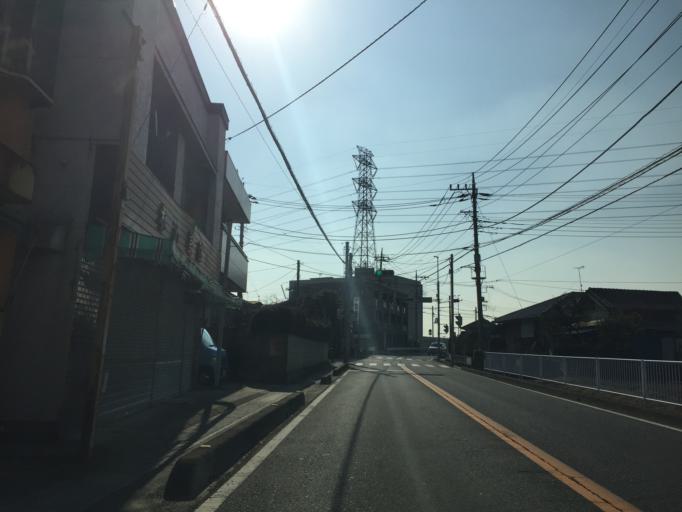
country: JP
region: Saitama
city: Shiki
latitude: 35.8431
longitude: 139.5831
